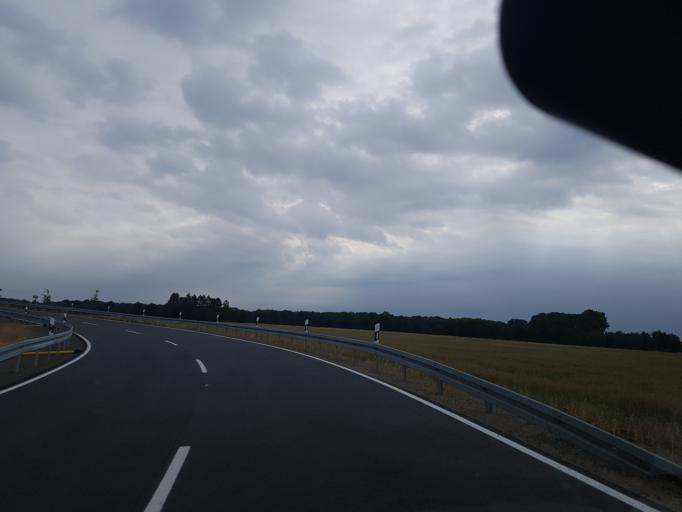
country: DE
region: Brandenburg
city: Schonewalde
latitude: 51.7044
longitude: 13.5984
